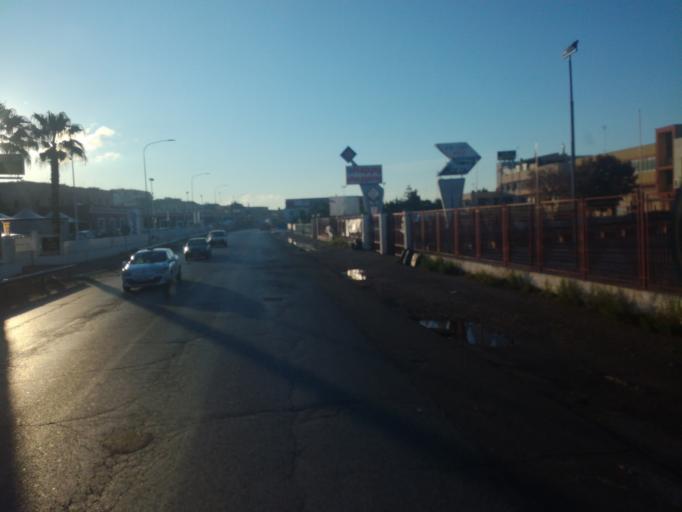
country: IT
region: Apulia
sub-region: Provincia di Taranto
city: Massafra
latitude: 40.5871
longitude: 17.1057
